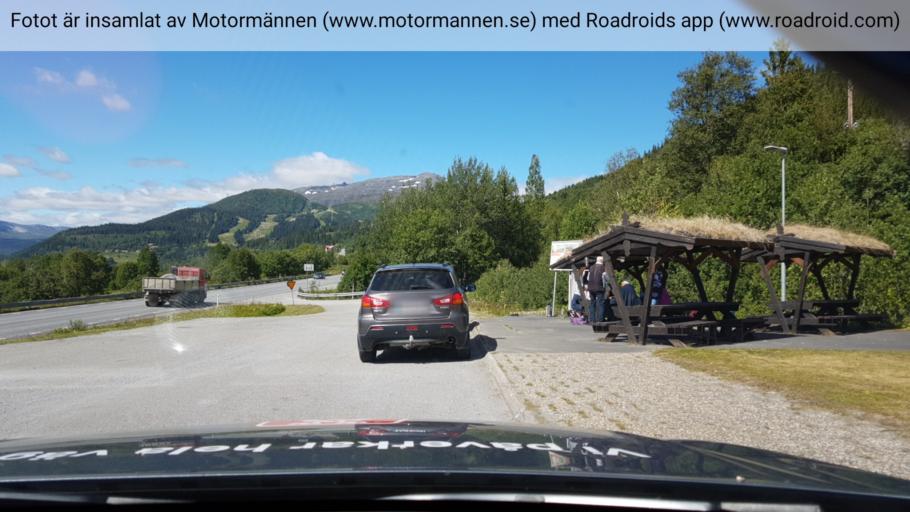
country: SE
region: Jaemtland
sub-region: Are Kommun
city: Are
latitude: 63.3736
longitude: 13.1616
